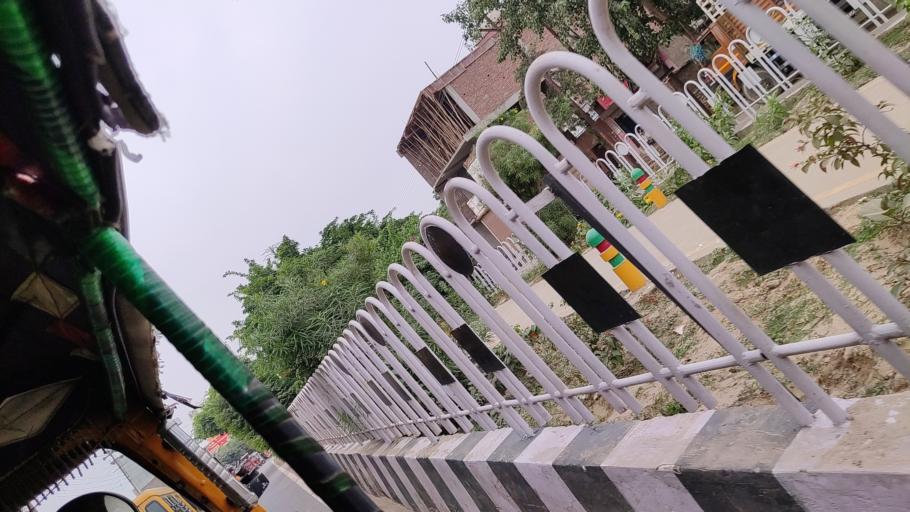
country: IN
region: Uttar Pradesh
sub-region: Mathura
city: Vrindavan
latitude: 27.5658
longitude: 77.6764
